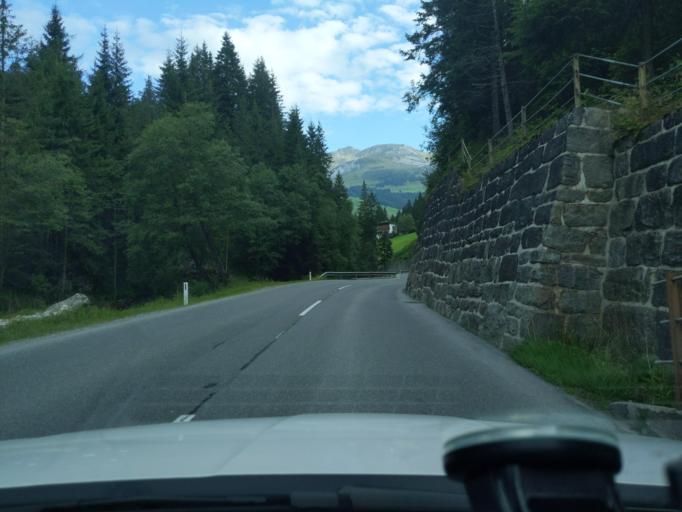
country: AT
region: Tyrol
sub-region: Politischer Bezirk Schwaz
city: Mayrhofen
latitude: 47.1445
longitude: 11.7193
